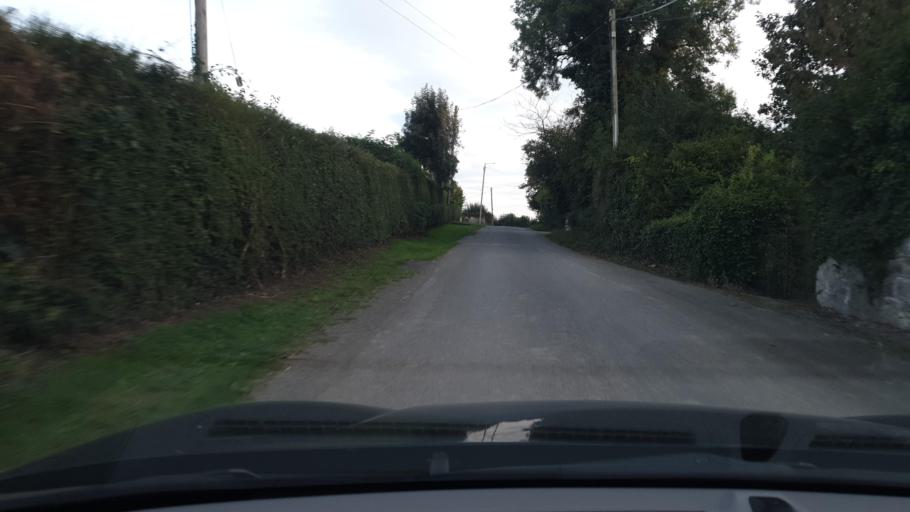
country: IE
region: Leinster
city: Balrothery
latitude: 53.5722
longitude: -6.2429
